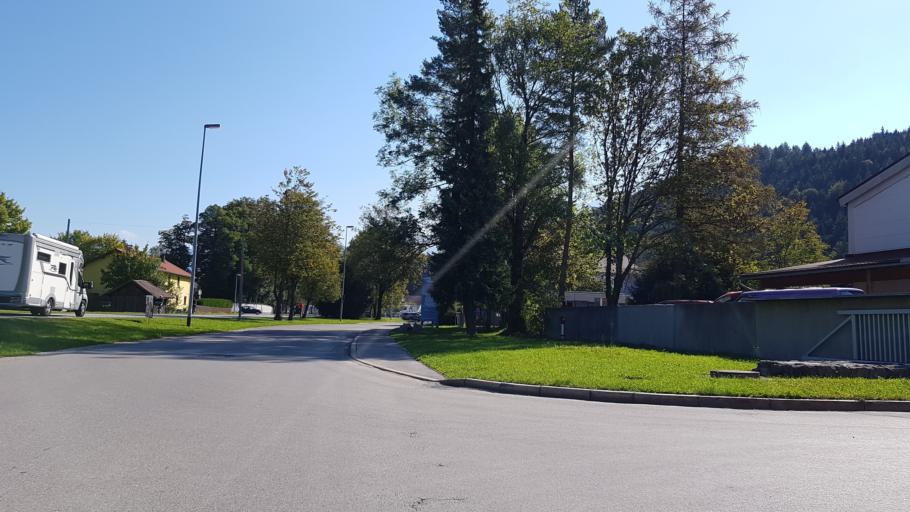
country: DE
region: Bavaria
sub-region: Swabia
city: Fuessen
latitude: 47.5686
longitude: 10.6733
